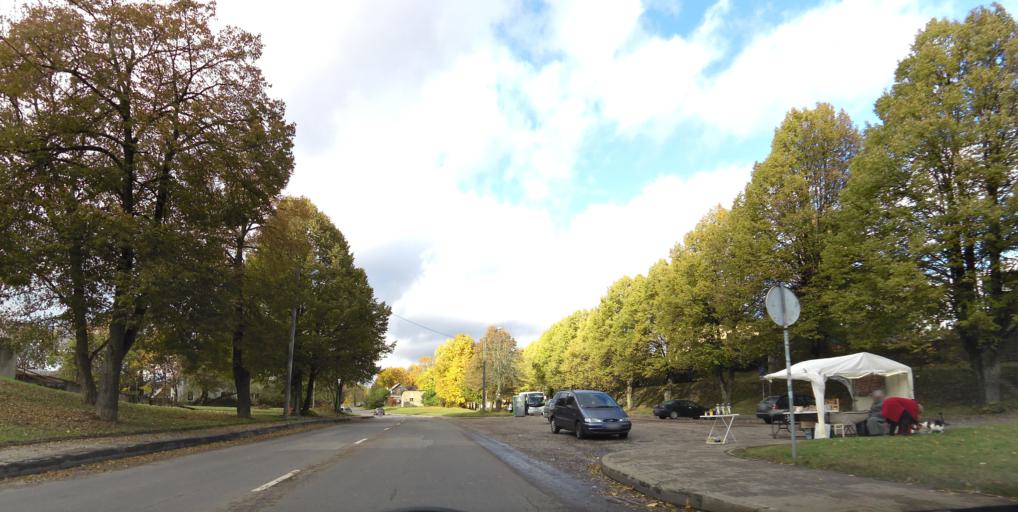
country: LT
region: Vilnius County
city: Rasos
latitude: 54.6706
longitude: 25.3009
